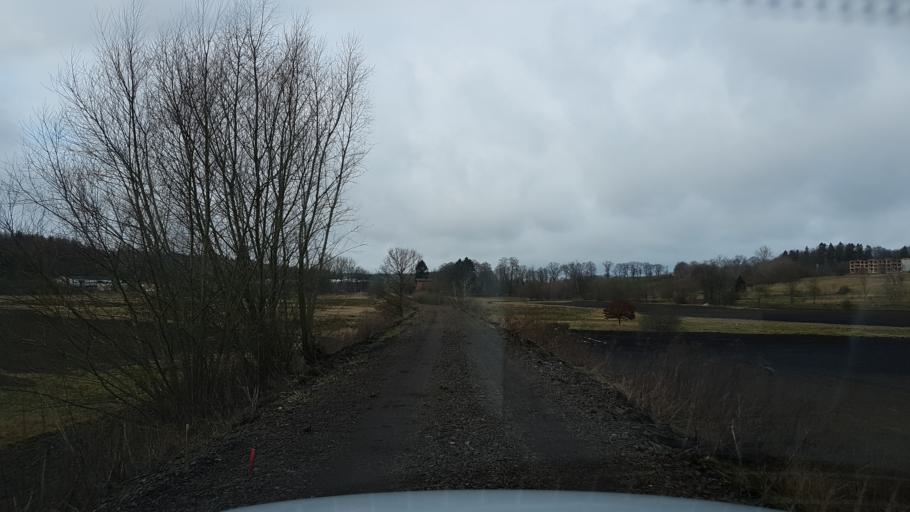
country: PL
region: West Pomeranian Voivodeship
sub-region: Powiat swidwinski
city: Polczyn-Zdroj
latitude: 53.7876
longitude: 16.0487
